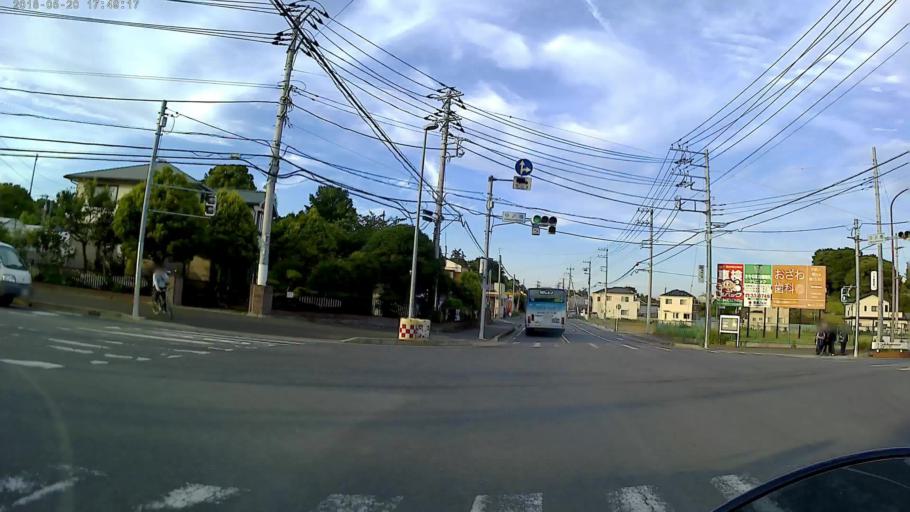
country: JP
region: Kanagawa
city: Oiso
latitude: 35.3419
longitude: 139.2934
